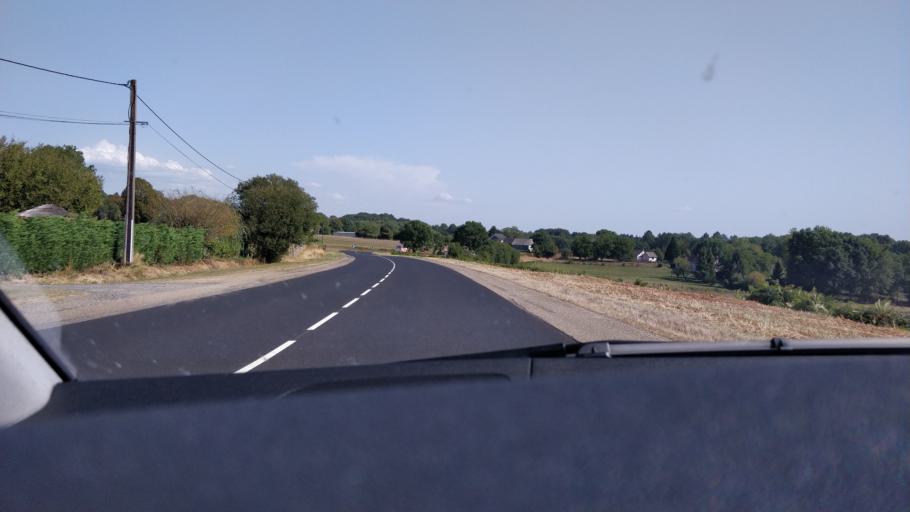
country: FR
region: Limousin
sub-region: Departement de la Correze
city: Uzerche
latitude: 45.4747
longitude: 1.5368
